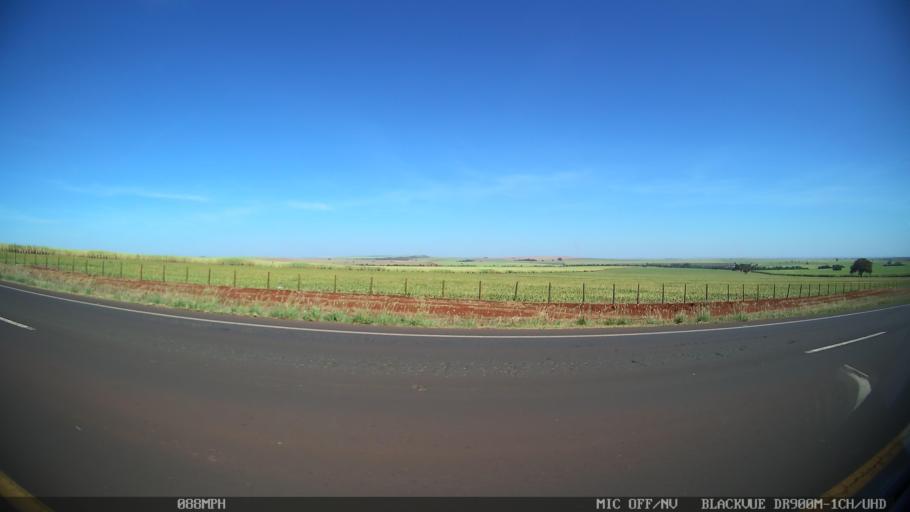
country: BR
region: Sao Paulo
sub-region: Ipua
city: Ipua
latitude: -20.4707
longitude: -48.1104
